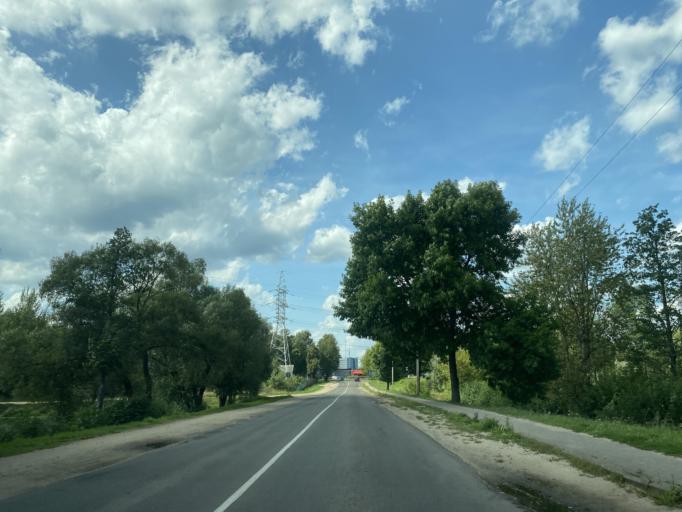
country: BY
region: Minsk
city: Horad Zhodzina
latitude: 54.1001
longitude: 28.3504
